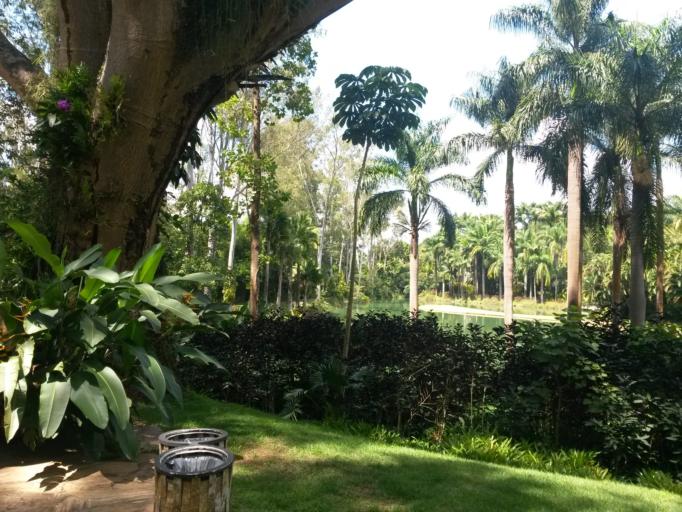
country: BR
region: Minas Gerais
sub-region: Brumadinho
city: Brumadinho
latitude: -20.1228
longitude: -44.2199
